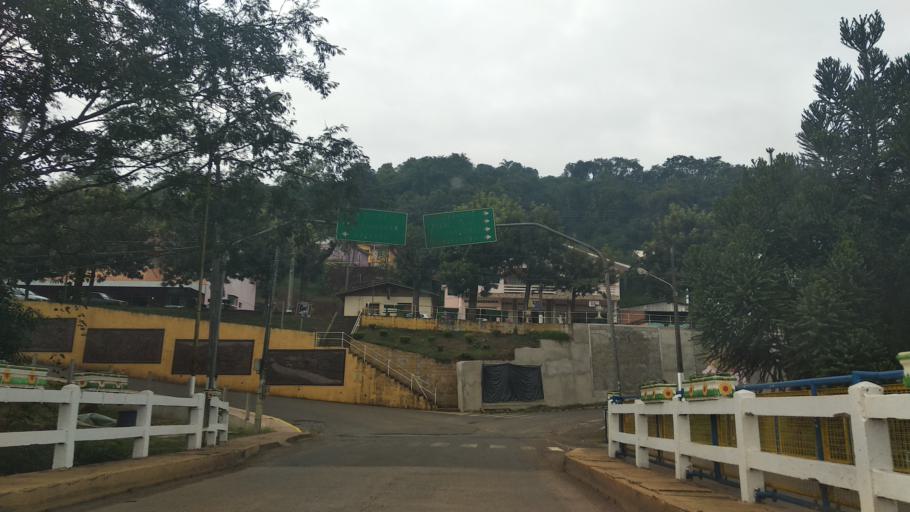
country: BR
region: Santa Catarina
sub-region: Videira
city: Videira
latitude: -27.0456
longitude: -51.2288
